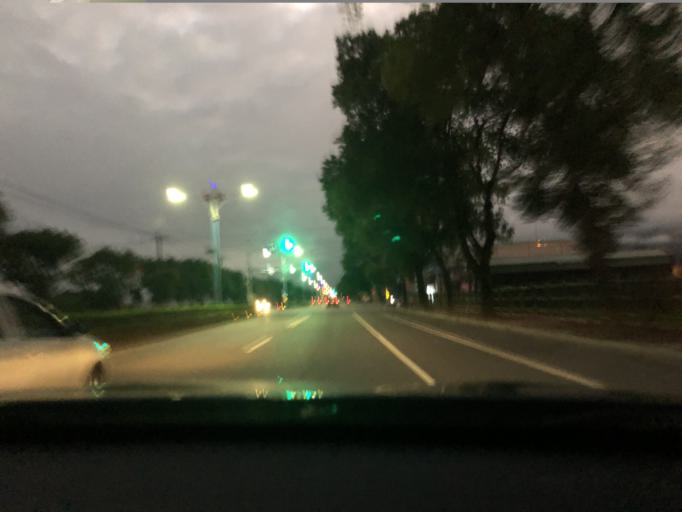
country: TW
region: Taiwan
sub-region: Hualien
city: Hualian
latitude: 23.9601
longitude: 121.5641
